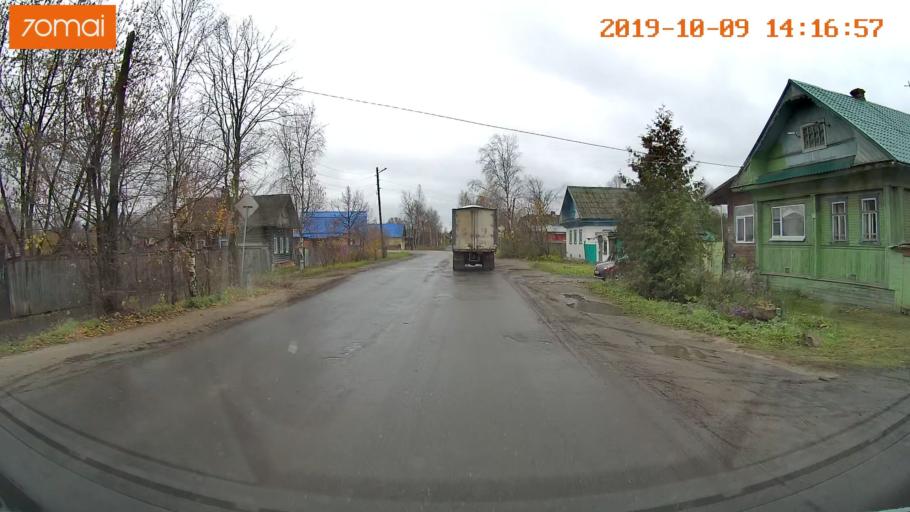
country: RU
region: Kostroma
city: Buy
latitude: 58.4812
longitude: 41.5222
